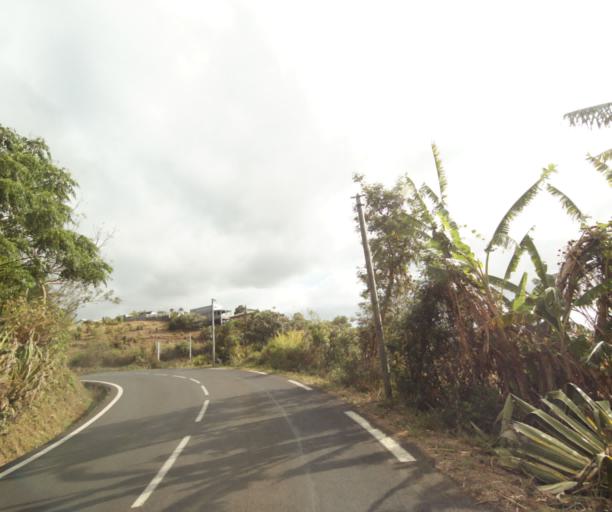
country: RE
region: Reunion
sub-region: Reunion
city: Saint-Paul
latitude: -21.0282
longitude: 55.3118
